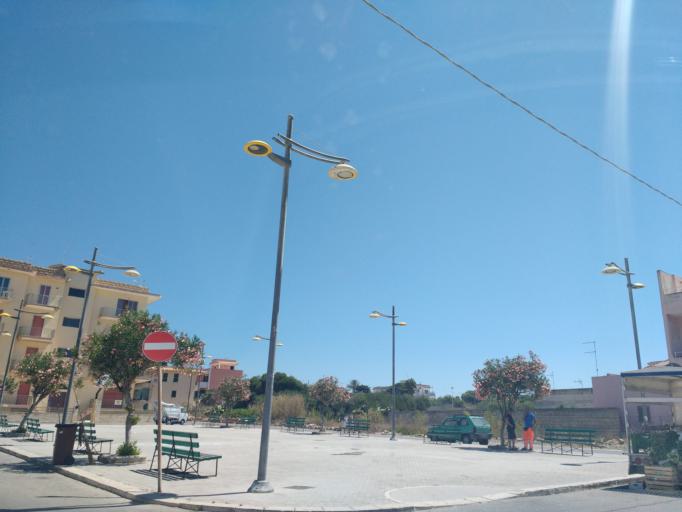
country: IT
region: Sicily
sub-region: Ragusa
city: Cava d'Aliga
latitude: 36.7265
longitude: 14.6884
